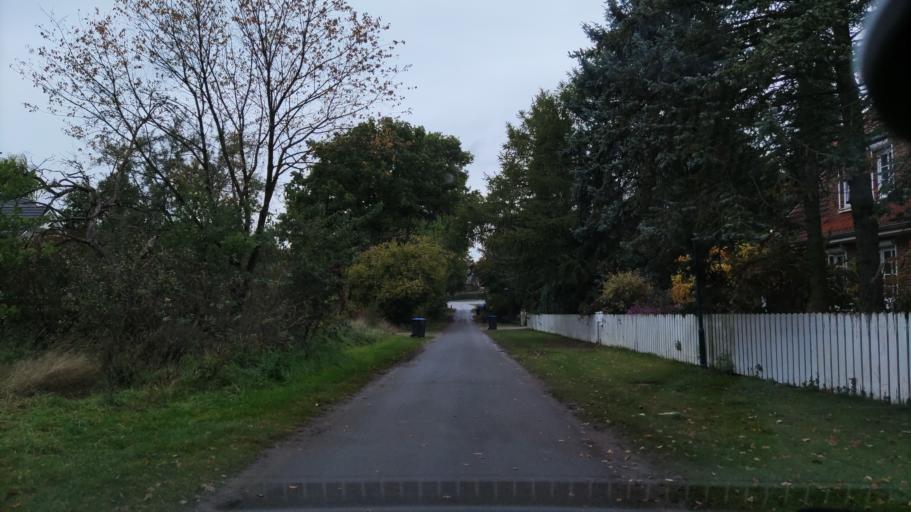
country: DE
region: Lower Saxony
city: Deutsch Evern
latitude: 53.1971
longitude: 10.4431
